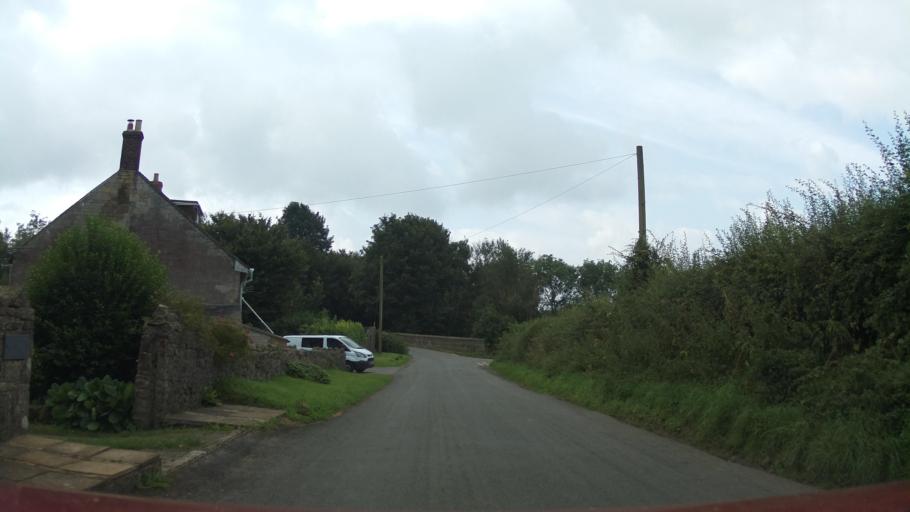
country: GB
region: England
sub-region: Somerset
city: Evercreech
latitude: 51.1810
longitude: -2.5068
